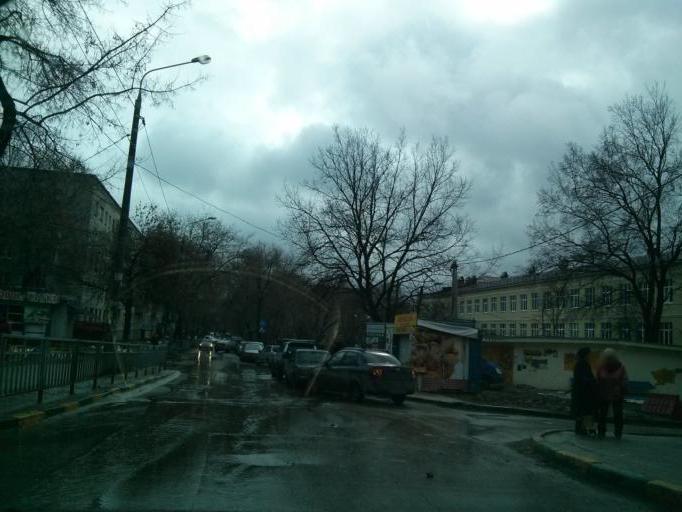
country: RU
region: Nizjnij Novgorod
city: Nizhniy Novgorod
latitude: 56.3199
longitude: 44.0470
